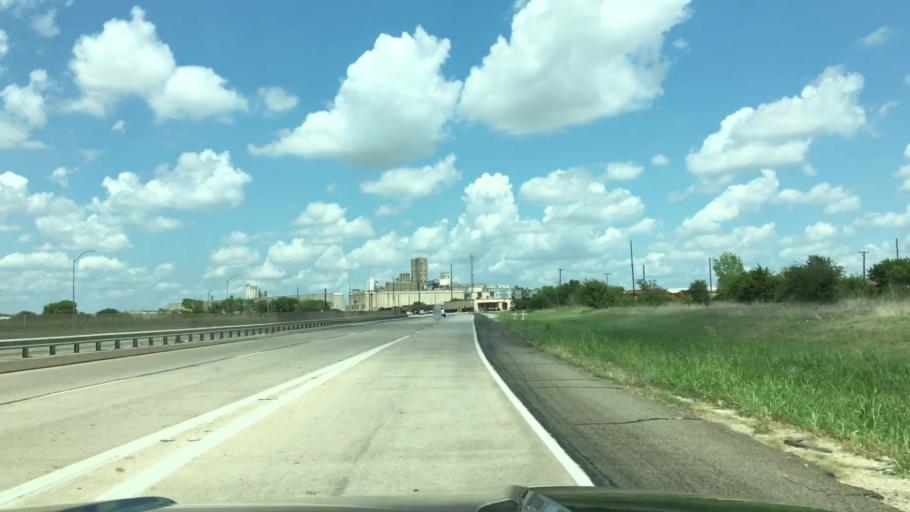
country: US
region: Texas
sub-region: Tarrant County
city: Saginaw
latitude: 32.8409
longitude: -97.3616
